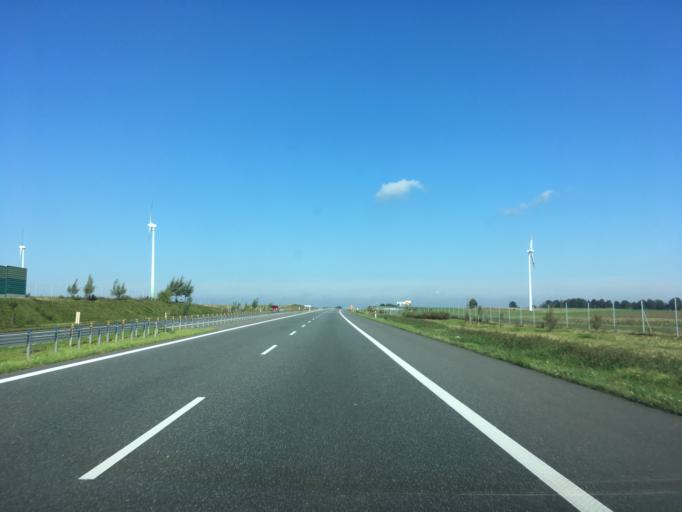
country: PL
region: Kujawsko-Pomorskie
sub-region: Powiat chelminski
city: Lisewo
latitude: 53.3718
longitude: 18.6933
